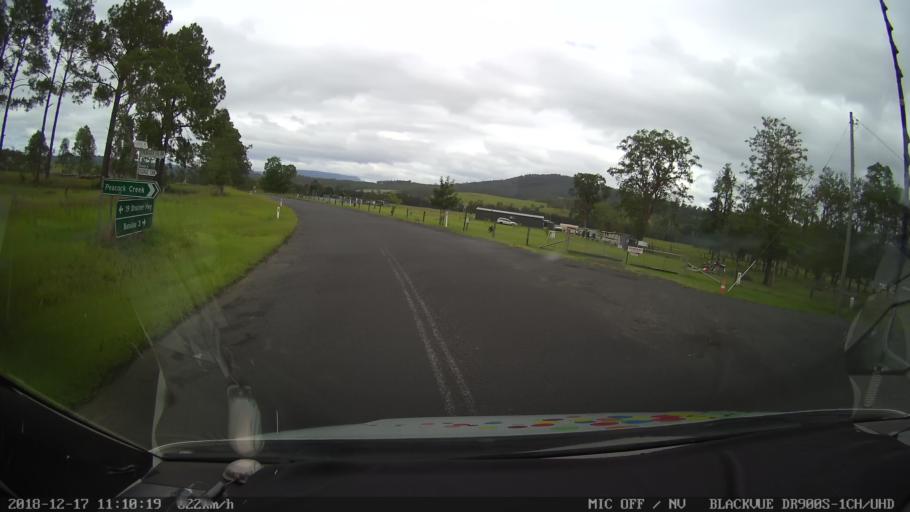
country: AU
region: New South Wales
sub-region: Kyogle
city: Kyogle
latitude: -28.7496
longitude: 152.6519
